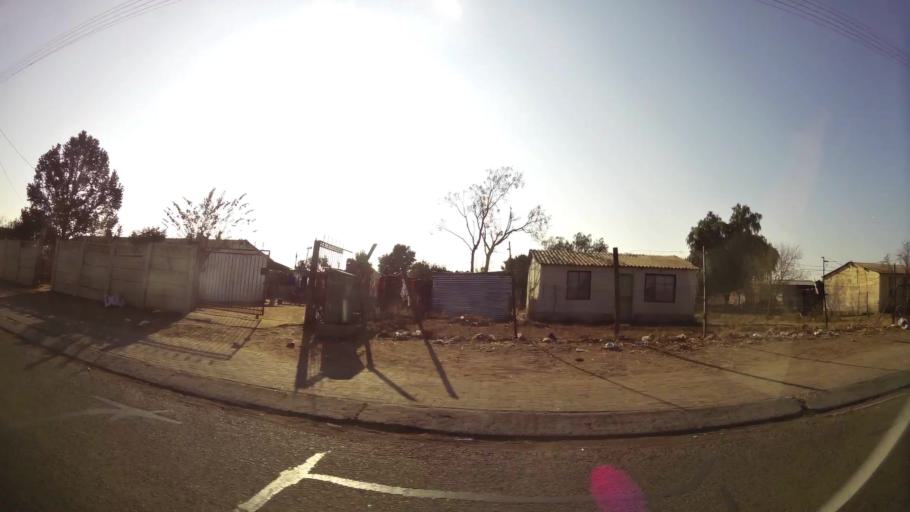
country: ZA
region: Orange Free State
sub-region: Mangaung Metropolitan Municipality
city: Bloemfontein
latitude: -29.1510
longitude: 26.2518
